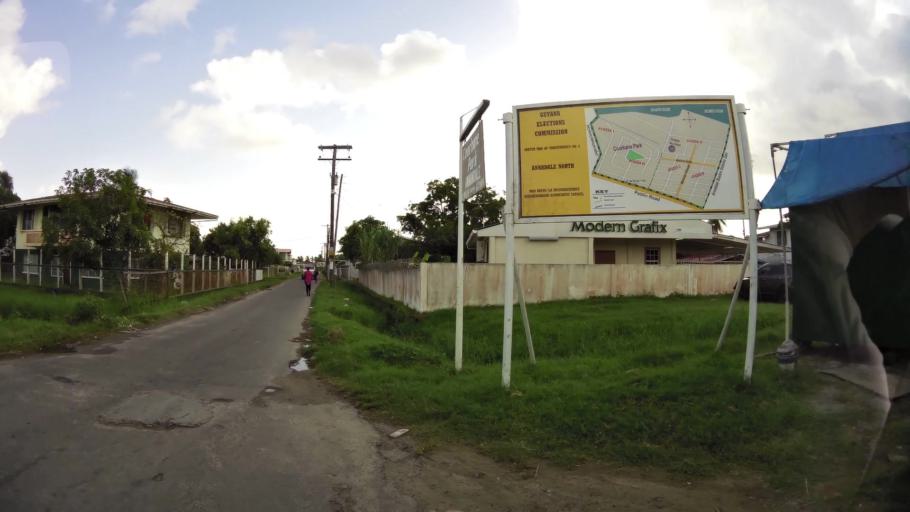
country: GY
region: Demerara-Mahaica
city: Georgetown
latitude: 6.7952
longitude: -58.0329
